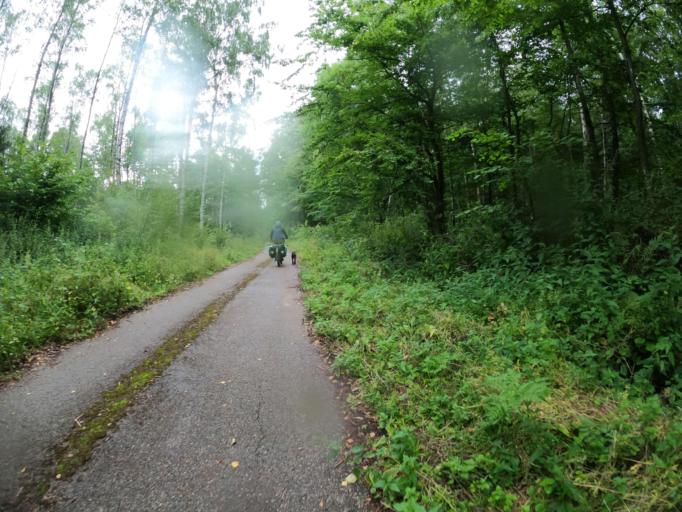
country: PL
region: West Pomeranian Voivodeship
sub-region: Powiat szczecinecki
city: Borne Sulinowo
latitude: 53.7081
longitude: 16.4927
